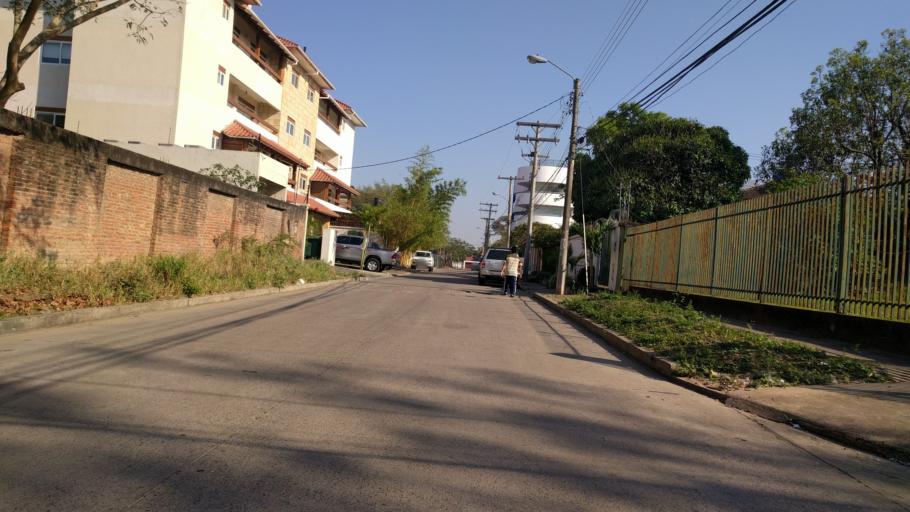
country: BO
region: Santa Cruz
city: Santa Cruz de la Sierra
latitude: -17.8082
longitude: -63.2078
